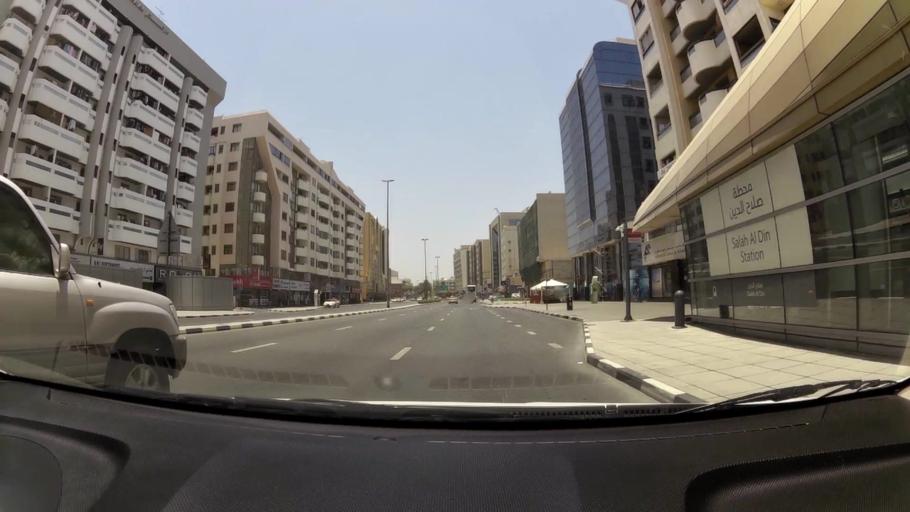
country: AE
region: Ash Shariqah
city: Sharjah
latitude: 25.2704
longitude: 55.3208
